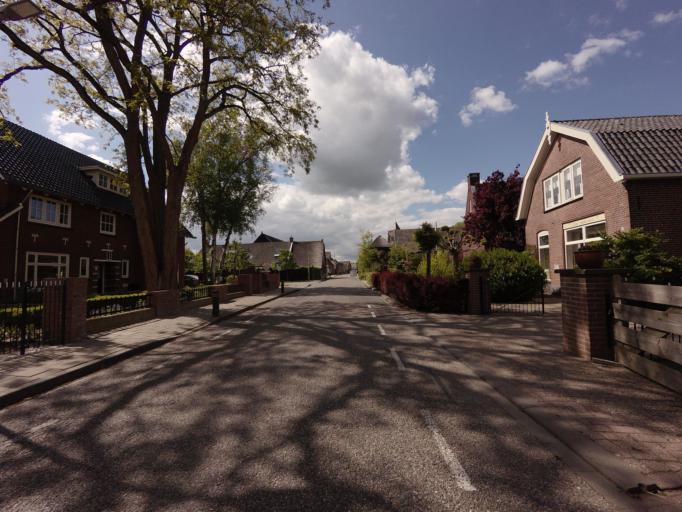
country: NL
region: South Holland
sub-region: Gemeente Leerdam
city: Leerdam
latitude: 51.9069
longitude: 5.0526
